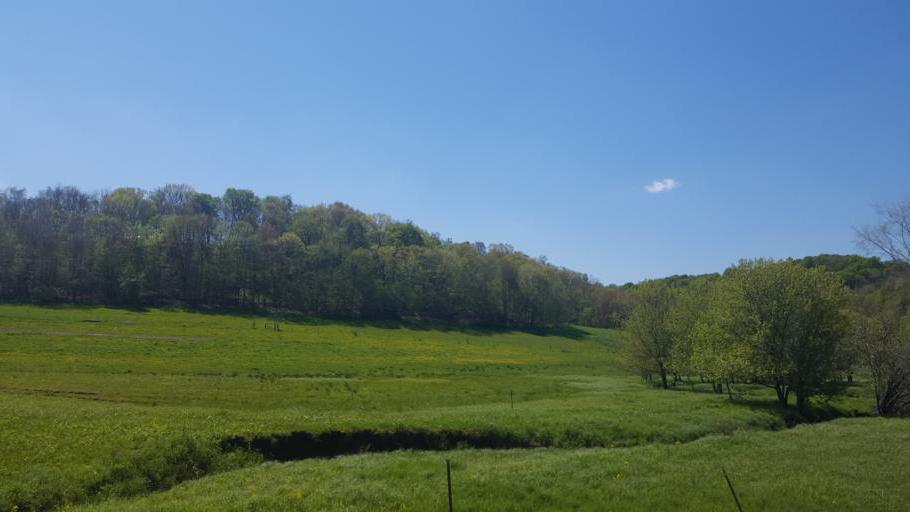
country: US
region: Wisconsin
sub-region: Vernon County
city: Hillsboro
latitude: 43.5714
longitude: -90.3862
